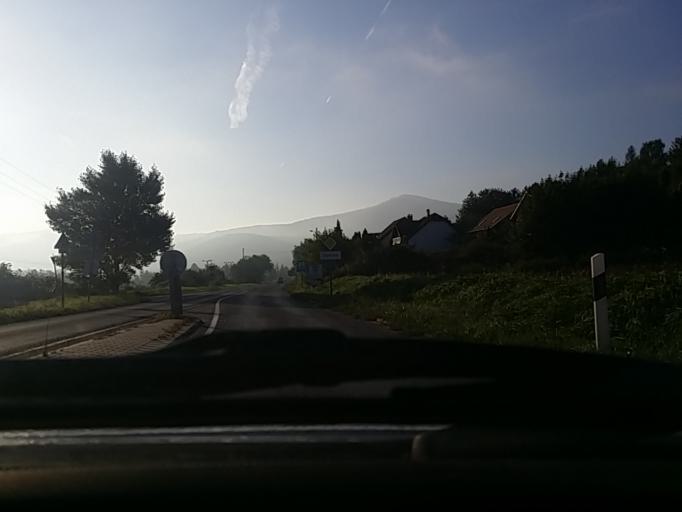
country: HU
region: Komarom-Esztergom
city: Pilismarot
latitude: 47.7728
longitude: 18.8988
